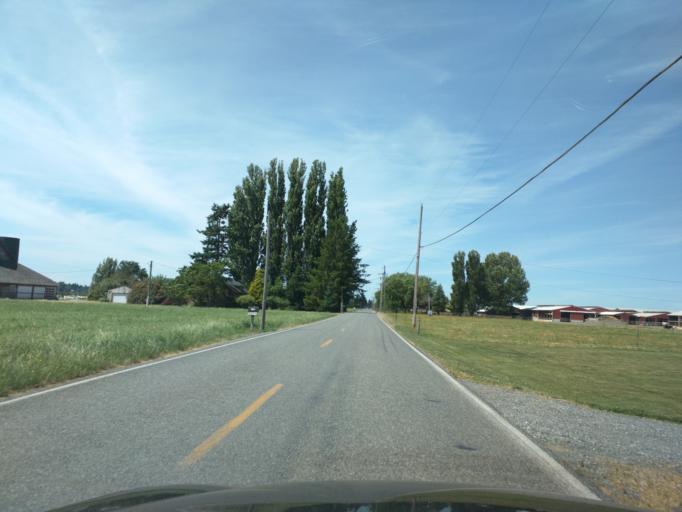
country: US
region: Washington
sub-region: Whatcom County
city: Lynden
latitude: 48.9277
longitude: -122.4123
